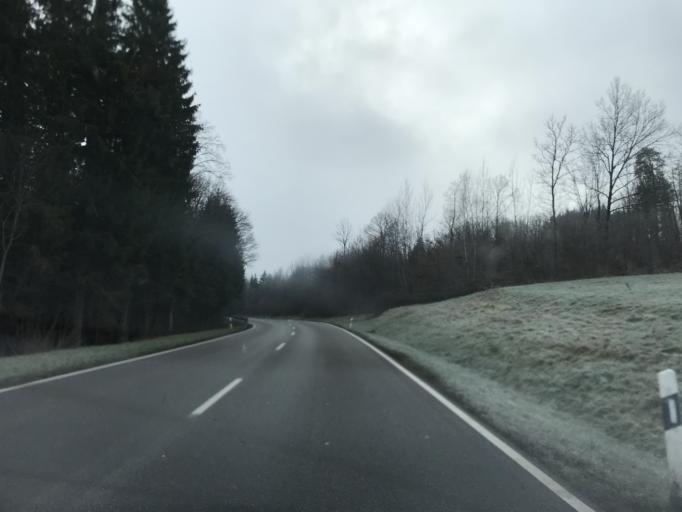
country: DE
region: Baden-Wuerttemberg
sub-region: Freiburg Region
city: Hasel
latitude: 47.6444
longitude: 7.8914
